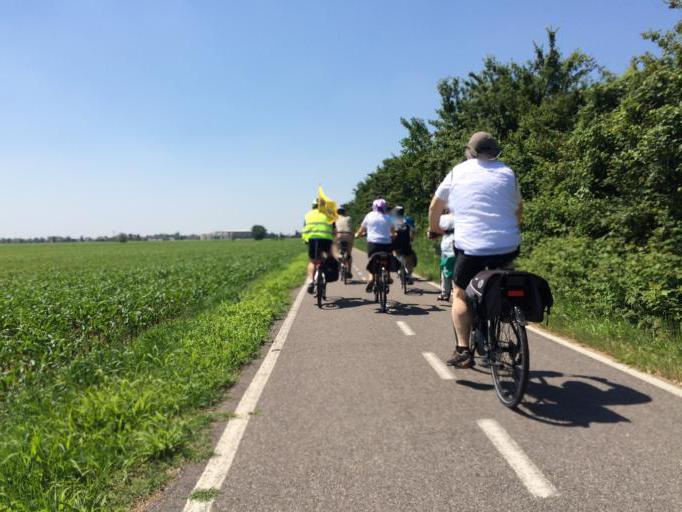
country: IT
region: Veneto
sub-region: Provincia di Vicenza
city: Ponte di Barbarano
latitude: 45.4045
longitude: 11.5753
